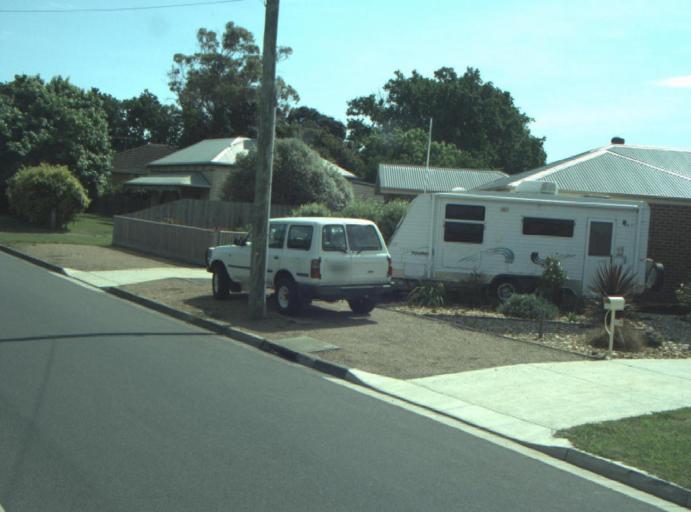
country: AU
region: Victoria
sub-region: Greater Geelong
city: Clifton Springs
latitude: -38.1704
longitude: 144.5713
